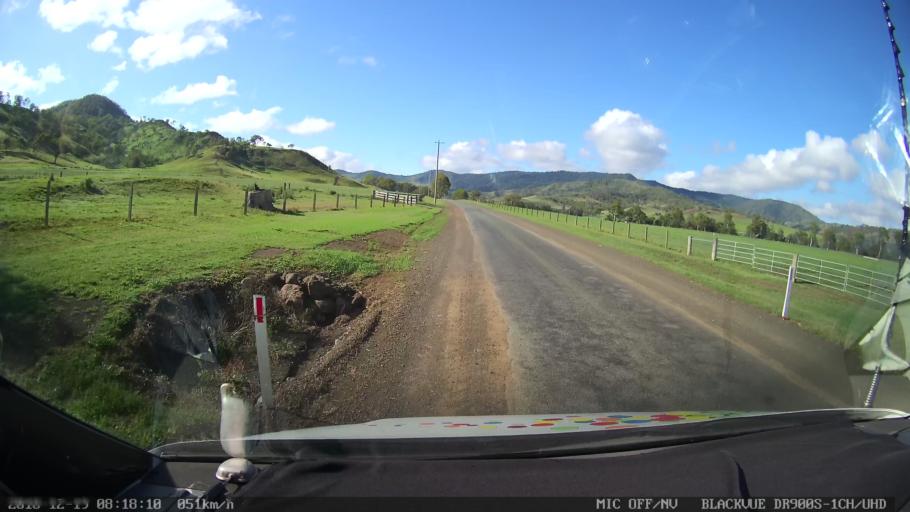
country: AU
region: New South Wales
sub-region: Kyogle
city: Kyogle
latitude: -28.2710
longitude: 152.9099
